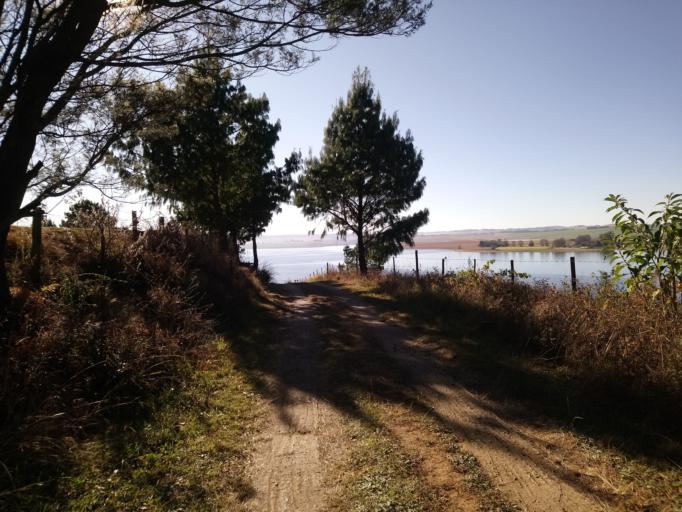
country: ZA
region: KwaZulu-Natal
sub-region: uMgungundlovu District Municipality
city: Mooirivier
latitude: -29.3347
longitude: 29.9204
